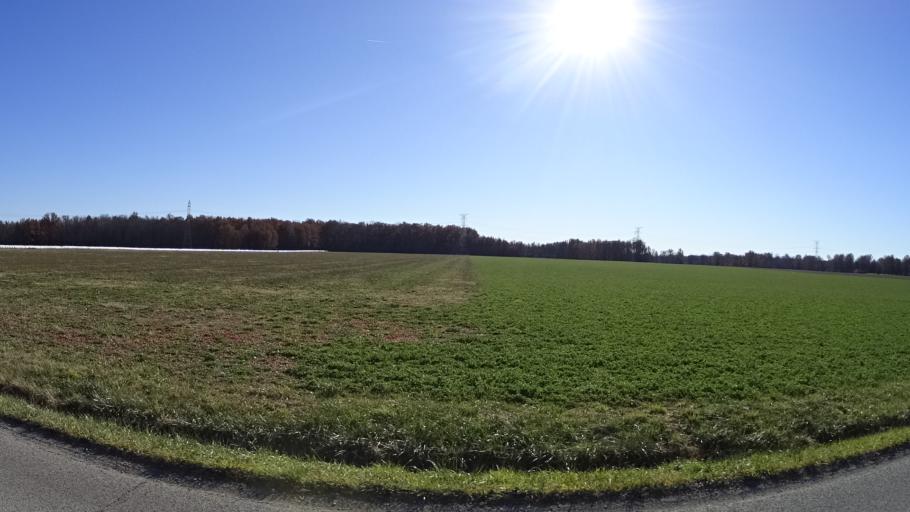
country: US
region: Ohio
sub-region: Lorain County
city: Grafton
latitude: 41.2850
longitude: -82.0930
